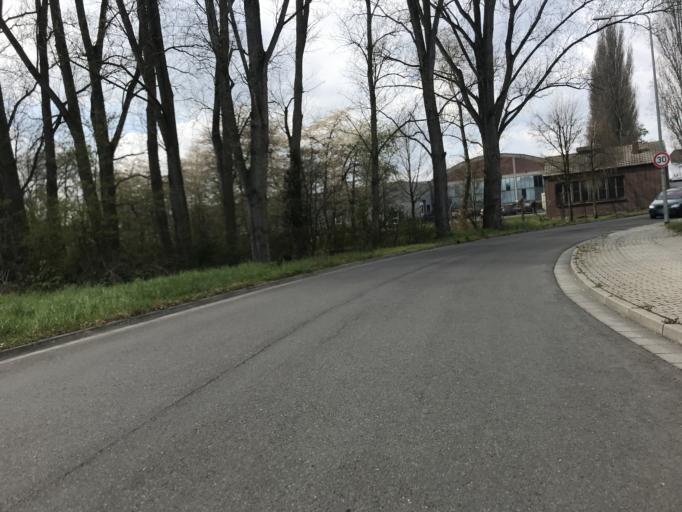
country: DE
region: Hesse
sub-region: Regierungsbezirk Darmstadt
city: Russelsheim
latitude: 50.0010
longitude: 8.4030
